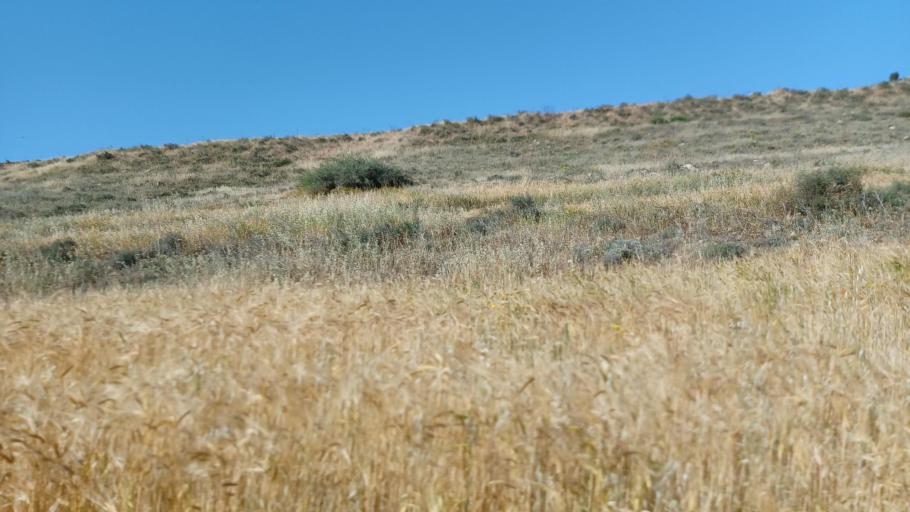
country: CY
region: Lefkosia
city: Mammari
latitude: 35.1642
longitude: 33.2369
